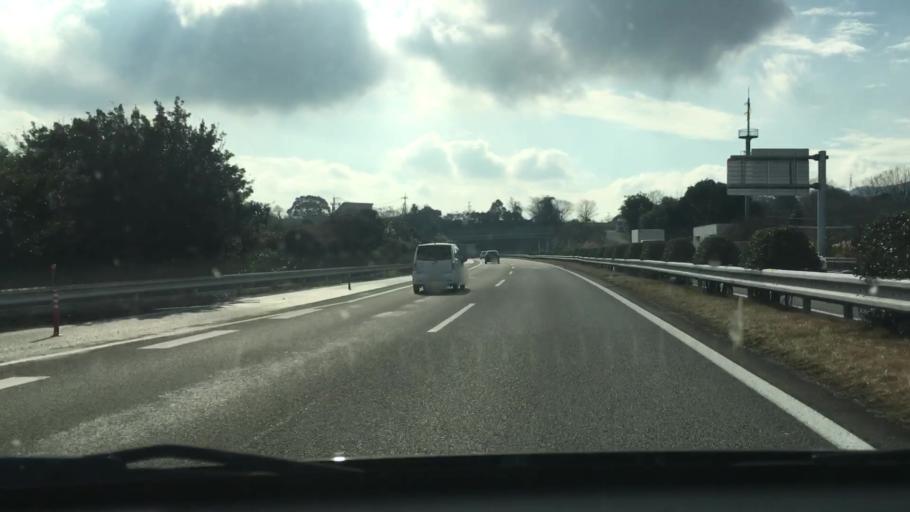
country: JP
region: Kumamoto
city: Uto
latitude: 32.6928
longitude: 130.7400
